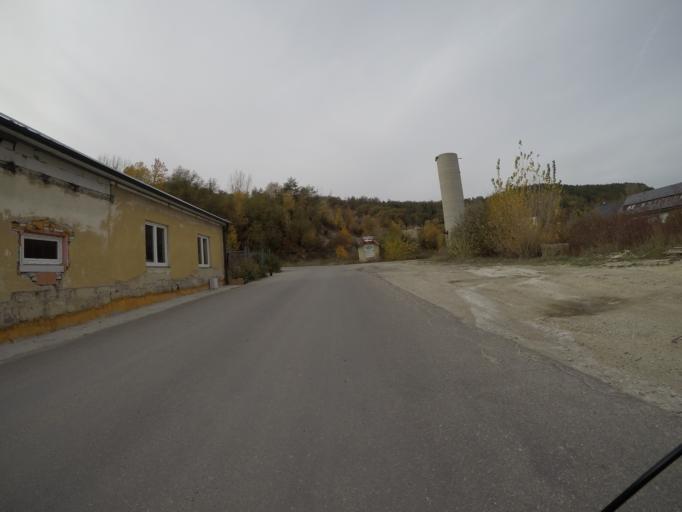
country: SK
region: Trenciansky
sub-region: Okres Nove Mesto nad Vahom
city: Nove Mesto nad Vahom
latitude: 48.7436
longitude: 17.8108
